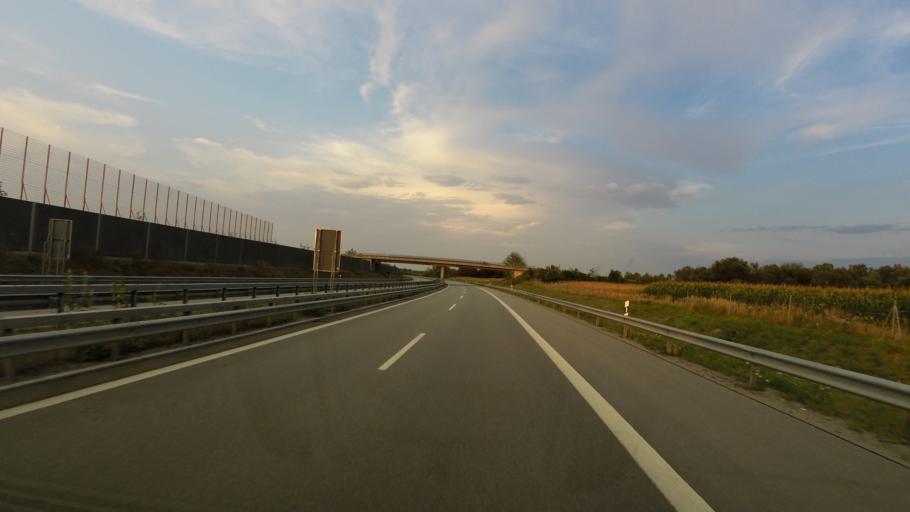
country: DE
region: Bavaria
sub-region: Lower Bavaria
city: Malching
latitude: 48.3059
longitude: 13.1856
